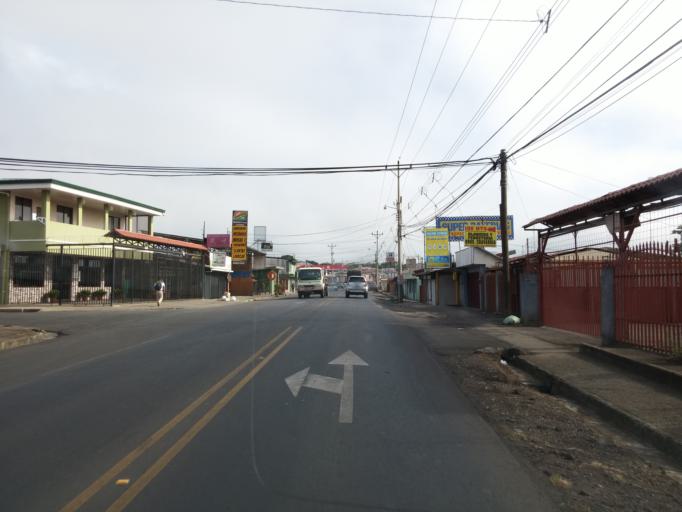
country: CR
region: Alajuela
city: San Ramon
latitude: 10.0966
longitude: -84.4687
